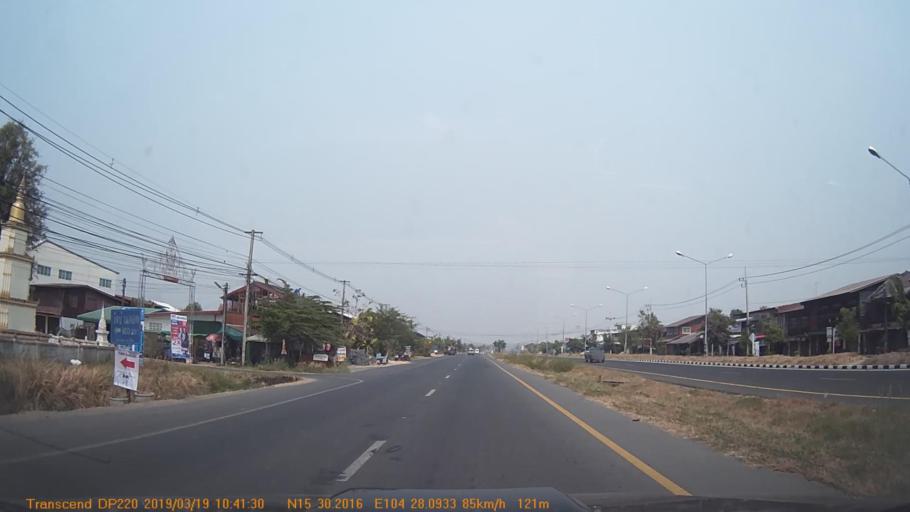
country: TH
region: Changwat Ubon Ratchathani
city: Khueang Nai
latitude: 15.5035
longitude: 104.4680
